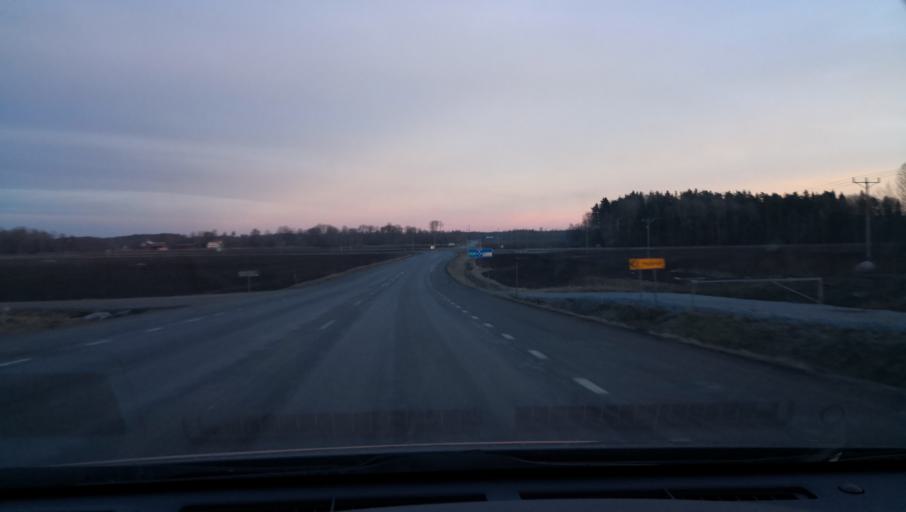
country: SE
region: OErebro
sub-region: Orebro Kommun
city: Vintrosa
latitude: 59.2430
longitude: 15.0457
